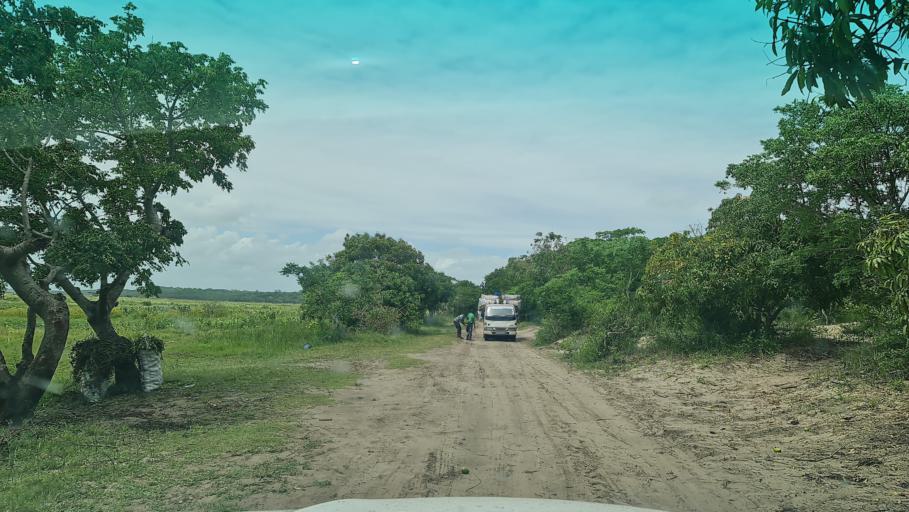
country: MZ
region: Maputo
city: Manhica
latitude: -25.5205
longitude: 32.8636
